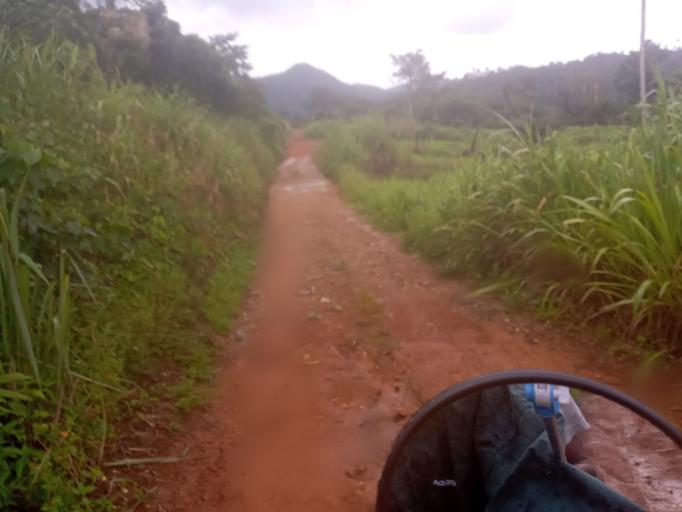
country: SL
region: Northern Province
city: Bumbuna
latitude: 8.9244
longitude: -11.7430
